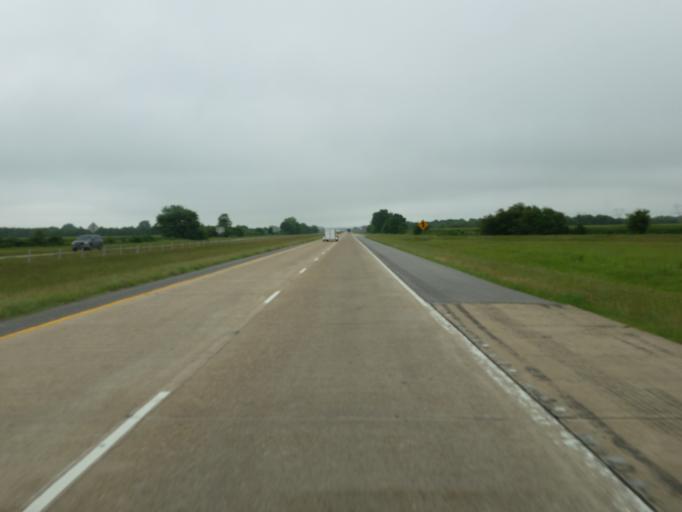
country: US
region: Mississippi
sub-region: Warren County
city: Vicksburg
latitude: 32.3296
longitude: -91.0230
